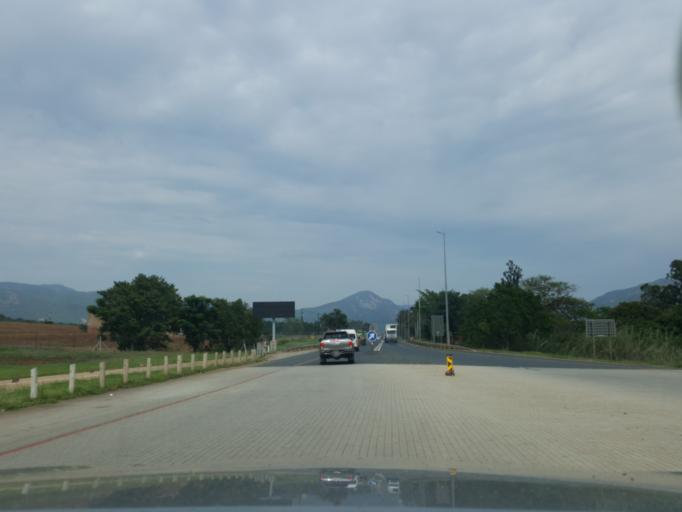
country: SZ
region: Hhohho
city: Ntfonjeni
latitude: -25.5364
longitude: 31.3433
